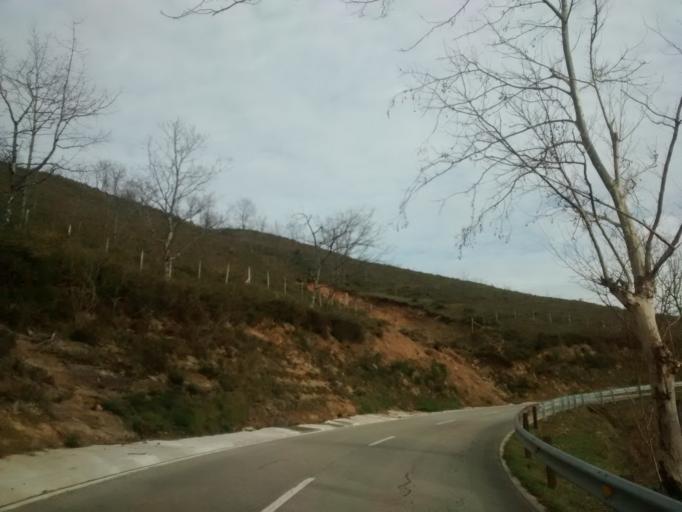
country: ES
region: Cantabria
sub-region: Provincia de Cantabria
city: Ruente
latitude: 43.2488
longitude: -4.3443
